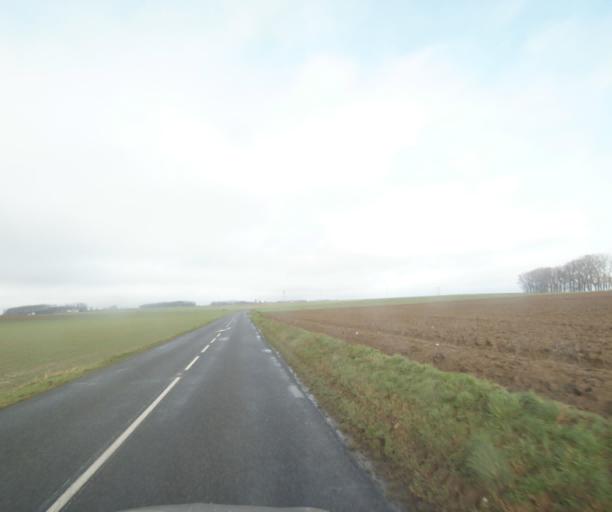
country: FR
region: Nord-Pas-de-Calais
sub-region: Departement du Nord
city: Artres
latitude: 50.2958
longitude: 3.5306
